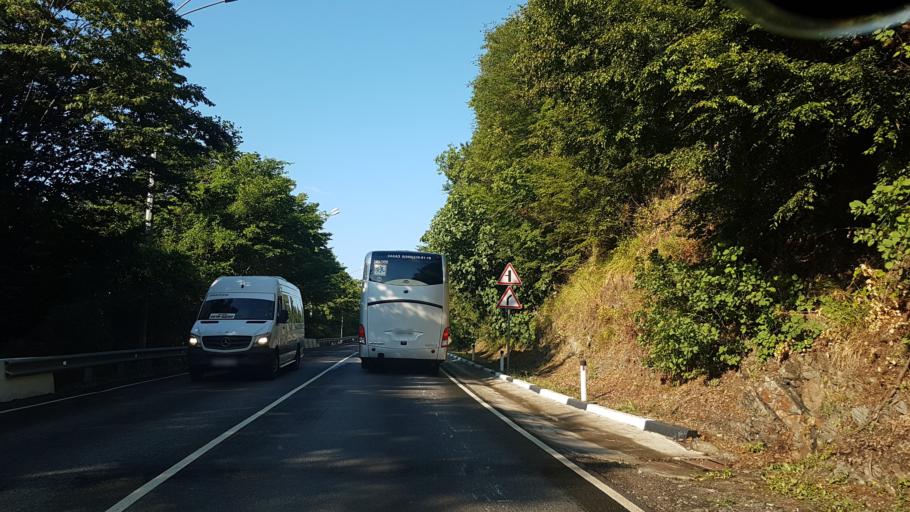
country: RU
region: Krasnodarskiy
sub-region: Sochi City
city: Lazarevskoye
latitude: 43.8435
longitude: 39.4160
